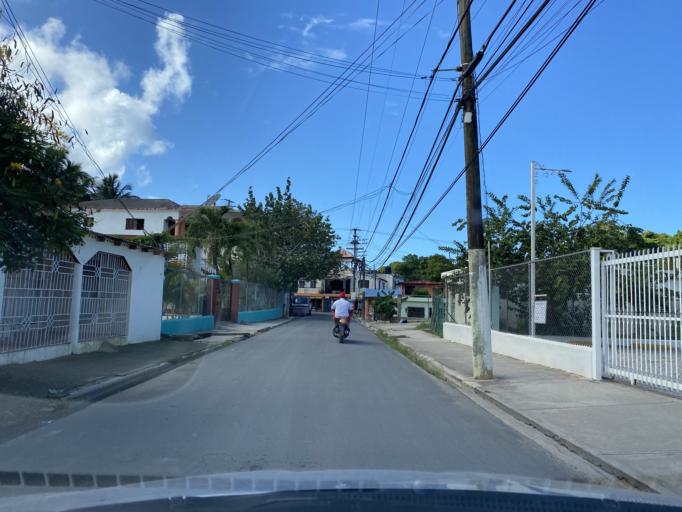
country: DO
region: Samana
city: Las Terrenas
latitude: 19.3116
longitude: -69.5458
